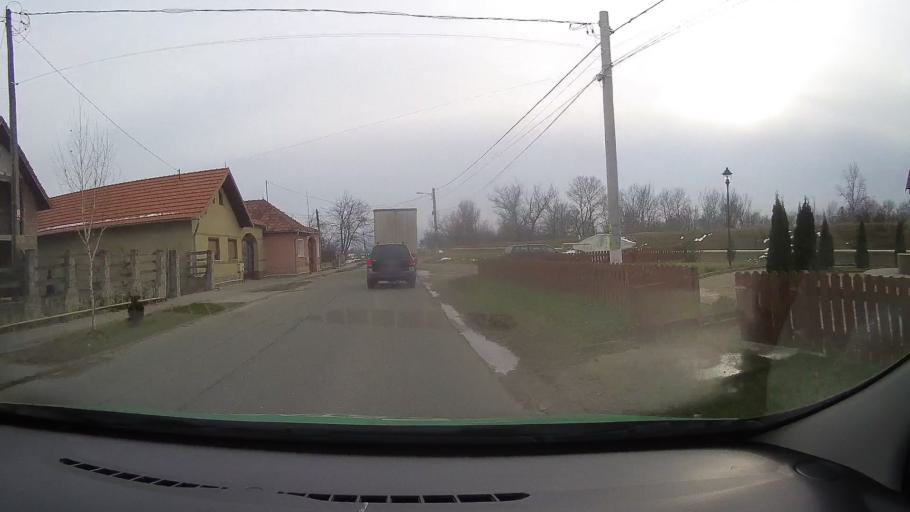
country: RO
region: Hunedoara
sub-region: Comuna Geoagiu
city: Geoagiu
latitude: 45.9001
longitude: 23.2246
